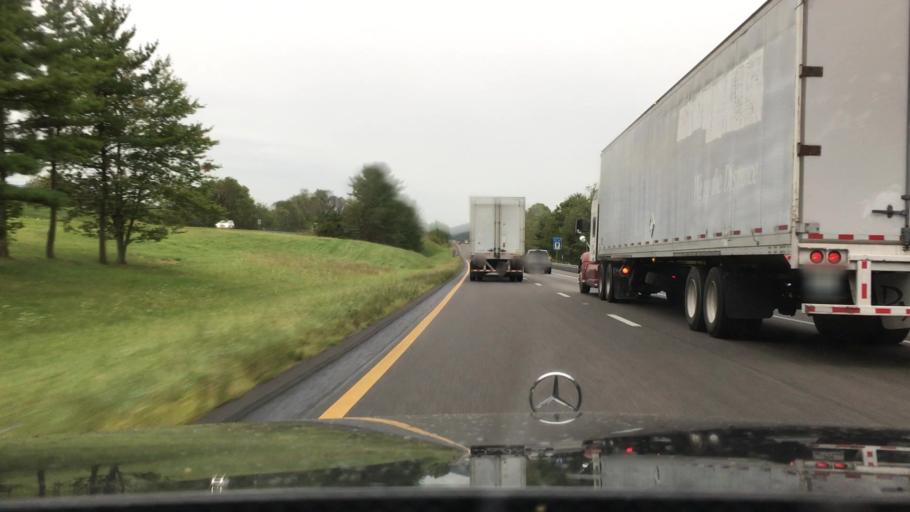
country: US
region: Virginia
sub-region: Smyth County
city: Atkins
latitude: 36.8937
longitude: -81.3590
